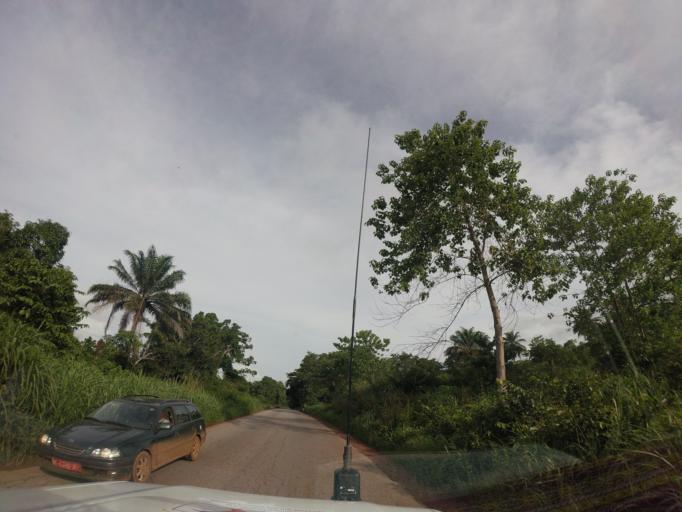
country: GN
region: Kindia
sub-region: Kindia
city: Kindia
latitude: 9.9036
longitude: -13.0068
